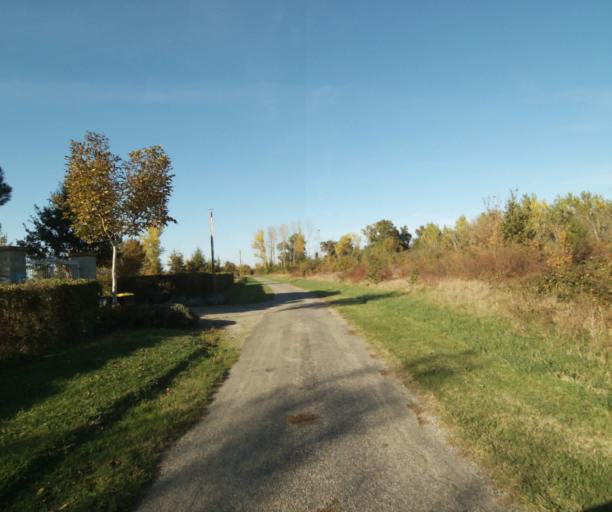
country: FR
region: Midi-Pyrenees
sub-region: Departement du Tarn-et-Garonne
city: Finhan
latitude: 43.9257
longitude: 1.2082
